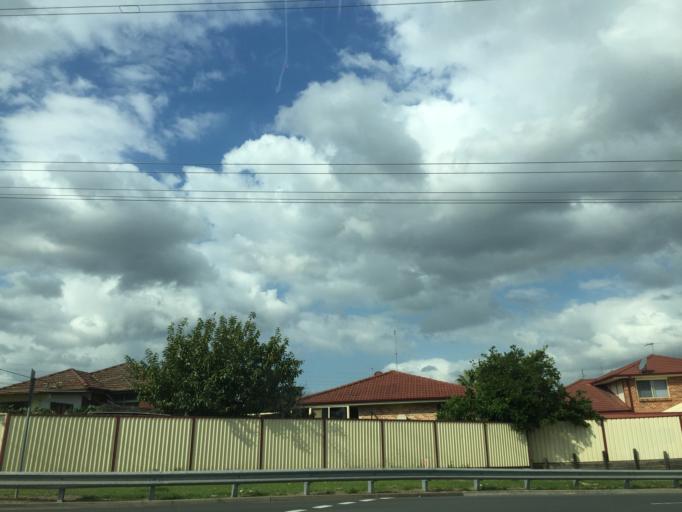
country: AU
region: New South Wales
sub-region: Blacktown
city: Blacktown
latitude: -33.7928
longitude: 150.8979
